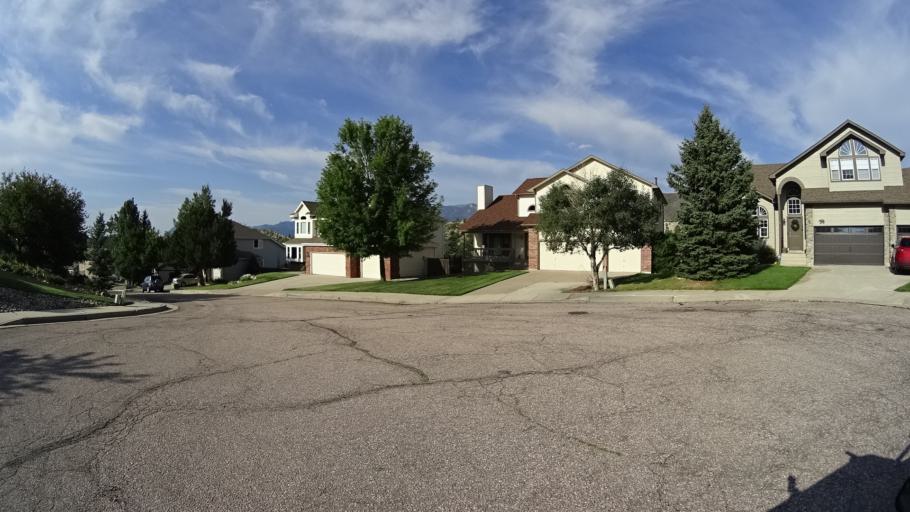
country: US
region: Colorado
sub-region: El Paso County
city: Air Force Academy
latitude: 38.9284
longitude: -104.8578
